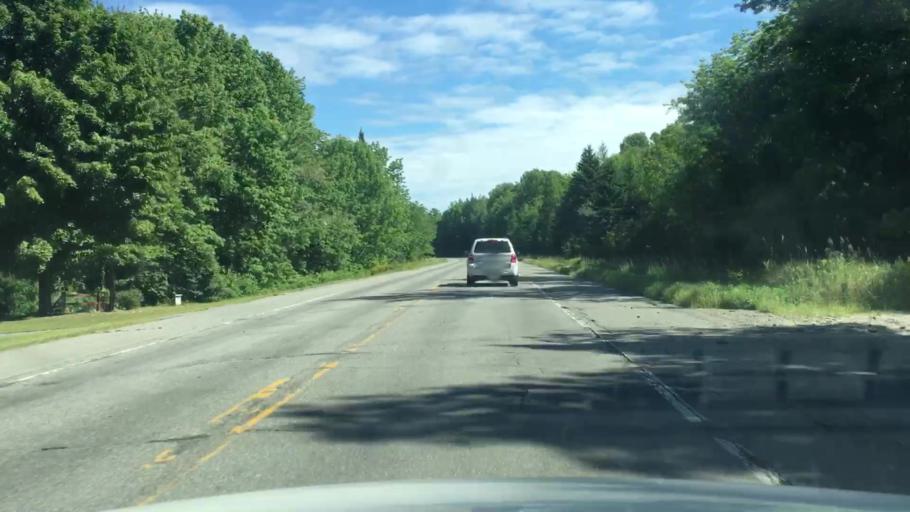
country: US
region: Maine
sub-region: Penobscot County
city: Dexter
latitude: 45.0505
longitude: -69.2638
